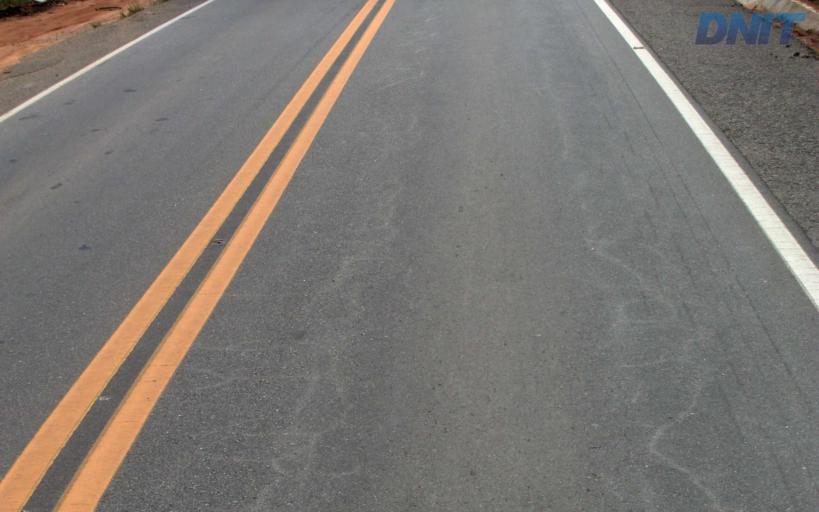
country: BR
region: Minas Gerais
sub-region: Governador Valadares
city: Governador Valadares
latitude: -18.9891
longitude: -42.1123
